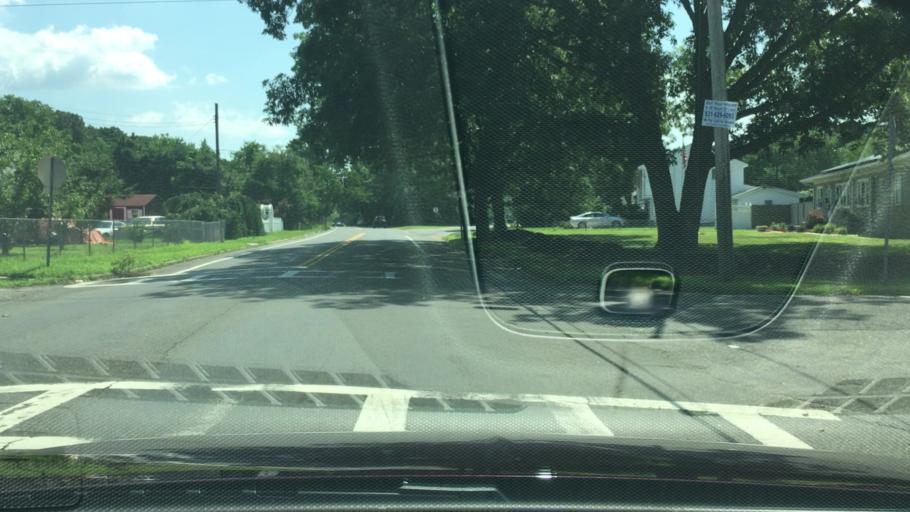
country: US
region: New York
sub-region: Suffolk County
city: Bay Wood
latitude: 40.7524
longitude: -73.2921
